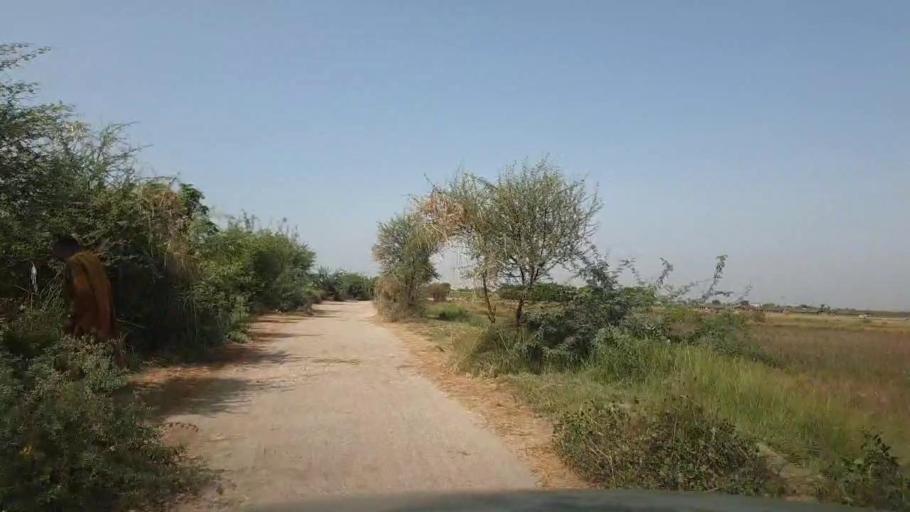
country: PK
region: Sindh
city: Tando Muhammad Khan
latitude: 25.1555
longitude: 68.3974
